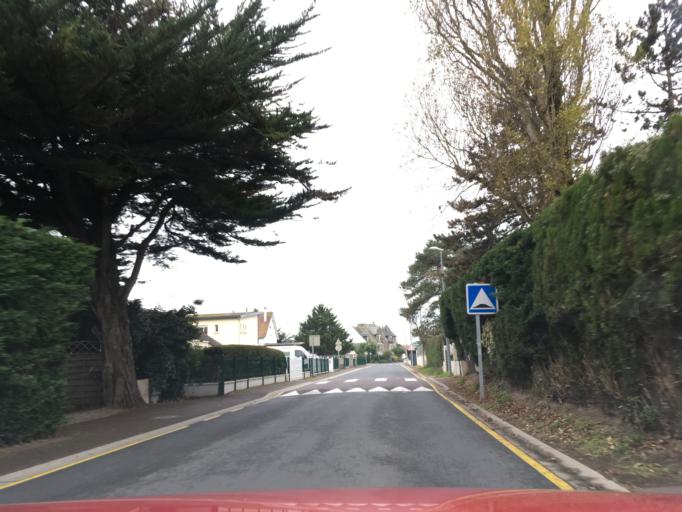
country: FR
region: Lower Normandy
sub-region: Departement de la Manche
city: Saint-Pair-sur-Mer
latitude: 48.7955
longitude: -1.5634
